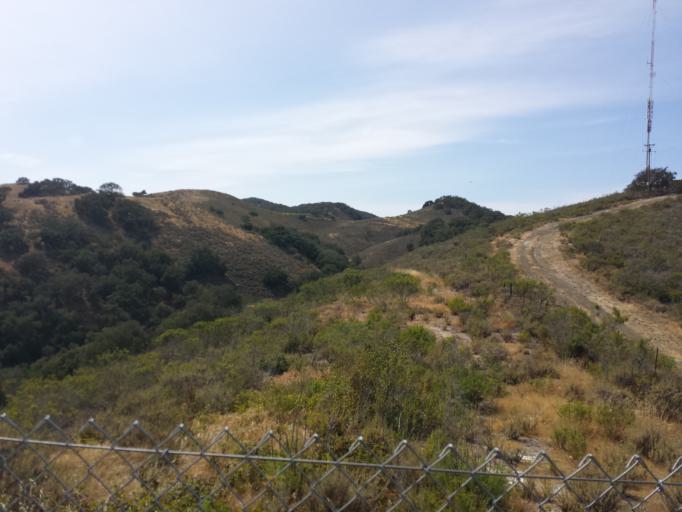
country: US
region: California
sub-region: San Luis Obispo County
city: Pismo Beach
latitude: 35.1552
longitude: -120.6361
